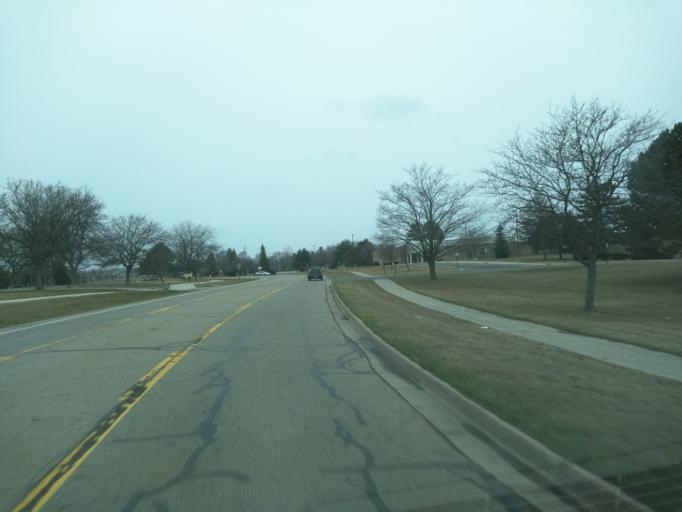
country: US
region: Michigan
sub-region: Eaton County
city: Waverly
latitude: 42.7287
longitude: -84.6211
